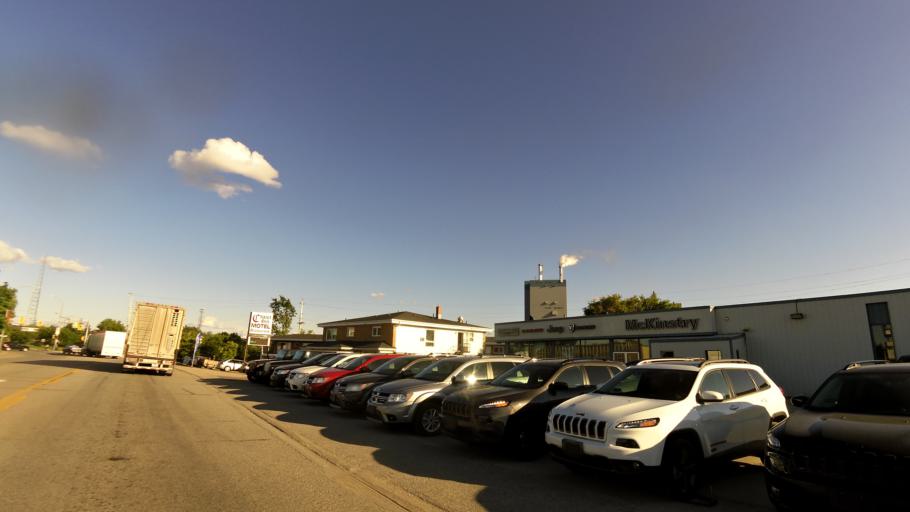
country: CA
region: Ontario
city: Dryden
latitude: 49.7873
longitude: -92.8463
